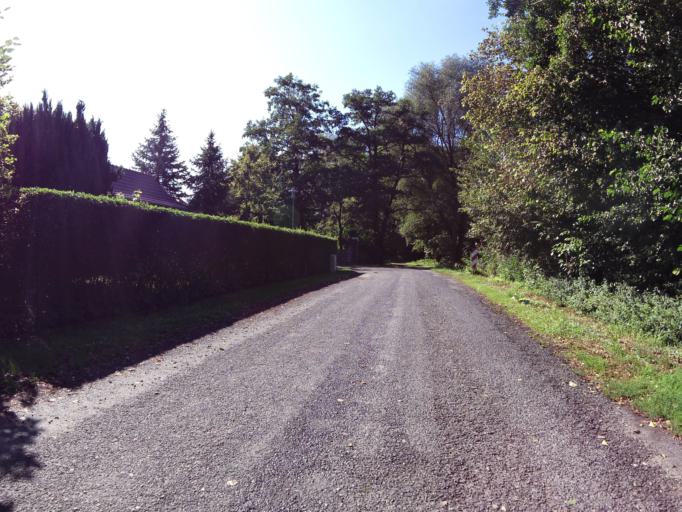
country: DE
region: Brandenburg
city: Storkow
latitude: 52.2498
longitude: 13.9389
